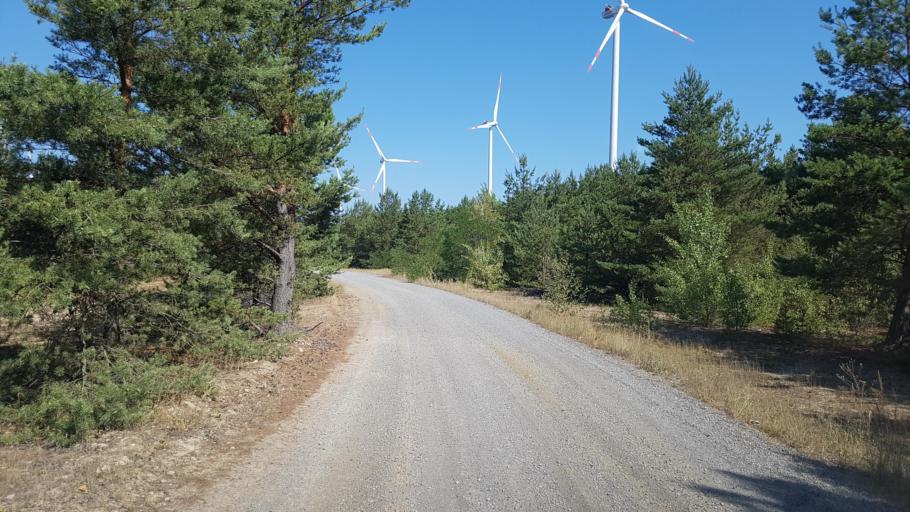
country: DE
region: Brandenburg
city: Schipkau
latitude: 51.5389
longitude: 13.8634
